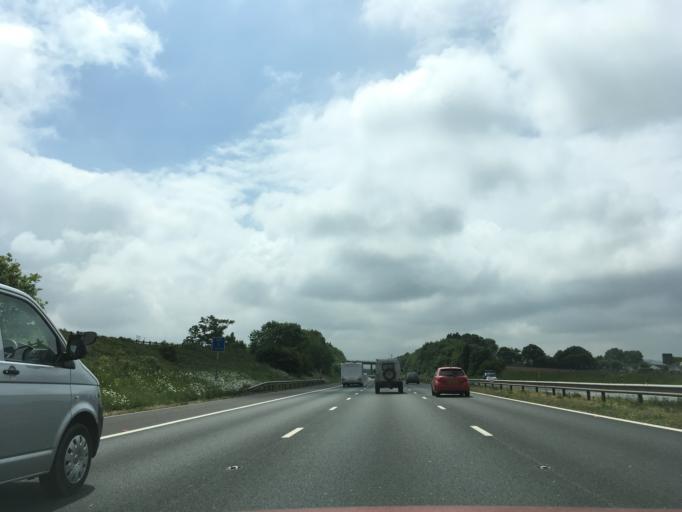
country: GB
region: England
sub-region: Devon
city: Cullompton
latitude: 50.8859
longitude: -3.3791
